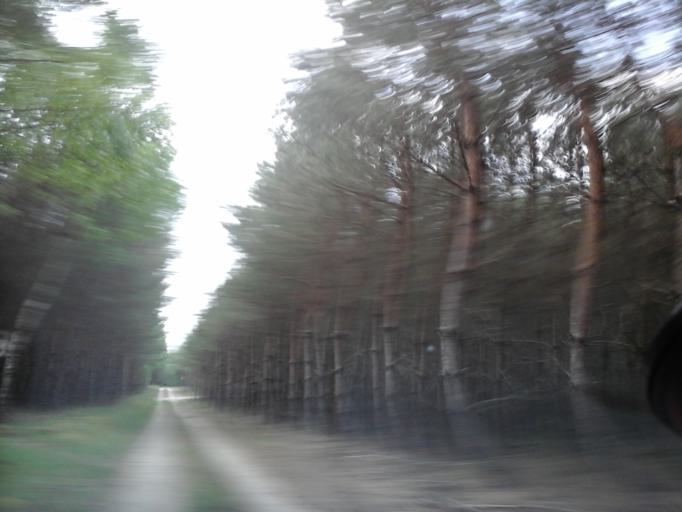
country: PL
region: West Pomeranian Voivodeship
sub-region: Powiat choszczenski
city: Drawno
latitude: 53.1216
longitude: 15.8980
